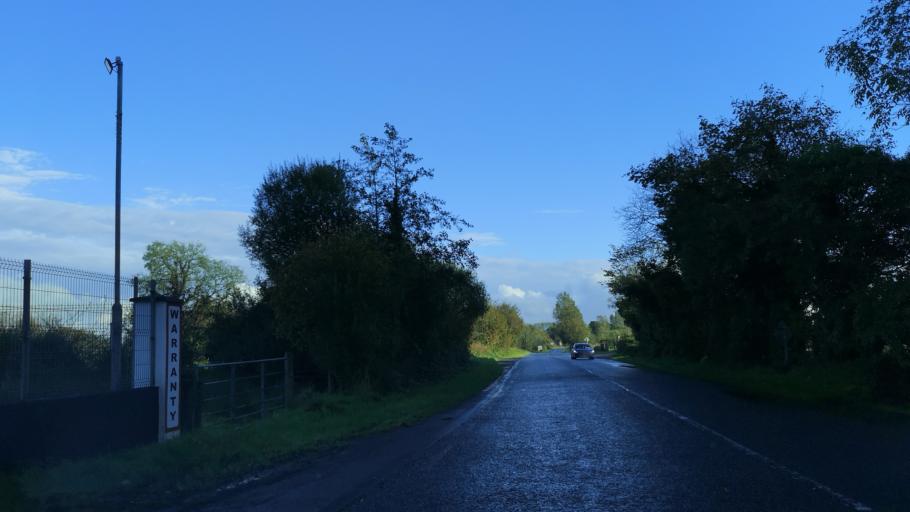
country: IE
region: Connaught
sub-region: Roscommon
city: Castlerea
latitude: 53.7859
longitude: -8.4897
